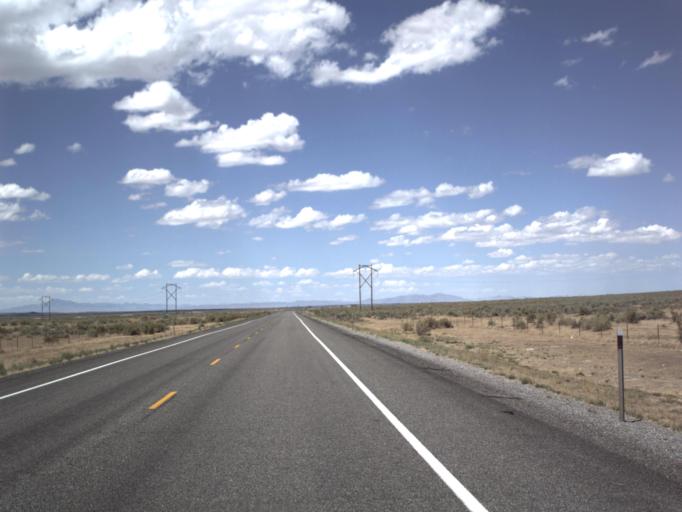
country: US
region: Utah
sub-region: Millard County
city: Fillmore
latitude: 39.1516
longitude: -112.3999
